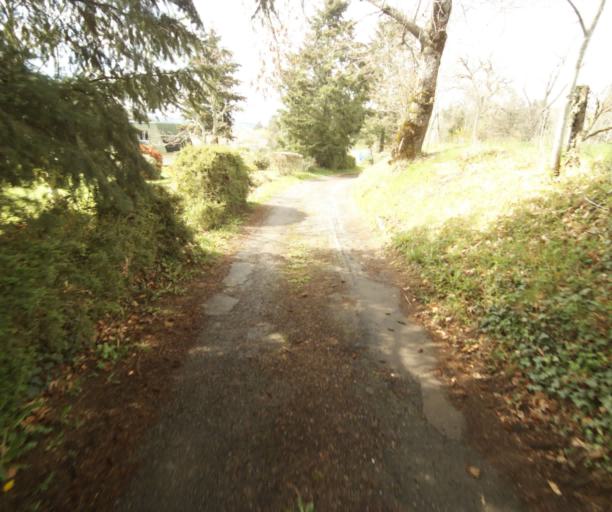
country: FR
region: Limousin
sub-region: Departement de la Correze
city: Tulle
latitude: 45.2844
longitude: 1.7420
